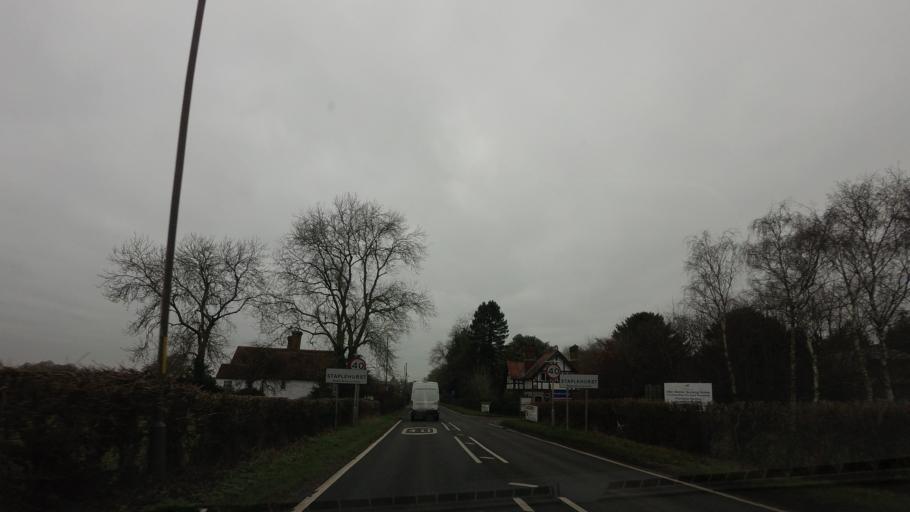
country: GB
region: England
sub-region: Kent
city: Staplehurst
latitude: 51.1507
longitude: 0.5521
